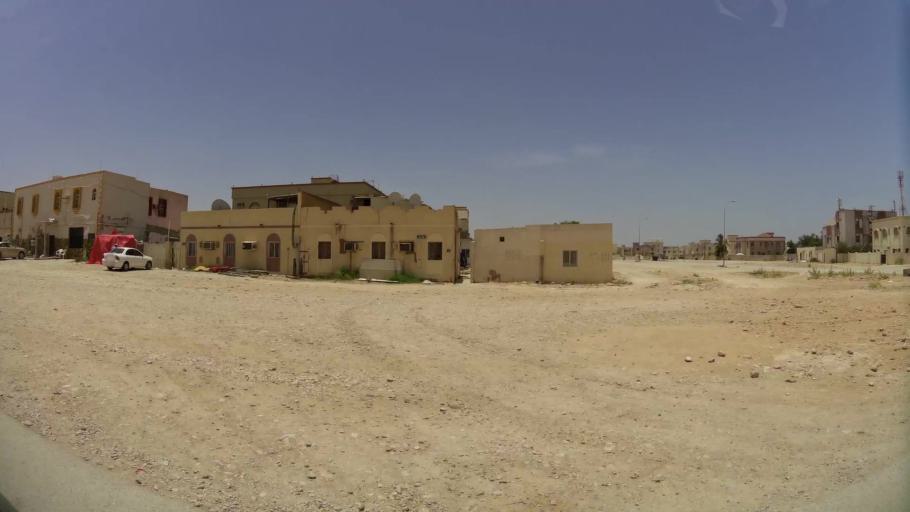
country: OM
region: Zufar
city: Salalah
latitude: 17.0795
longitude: 54.1522
